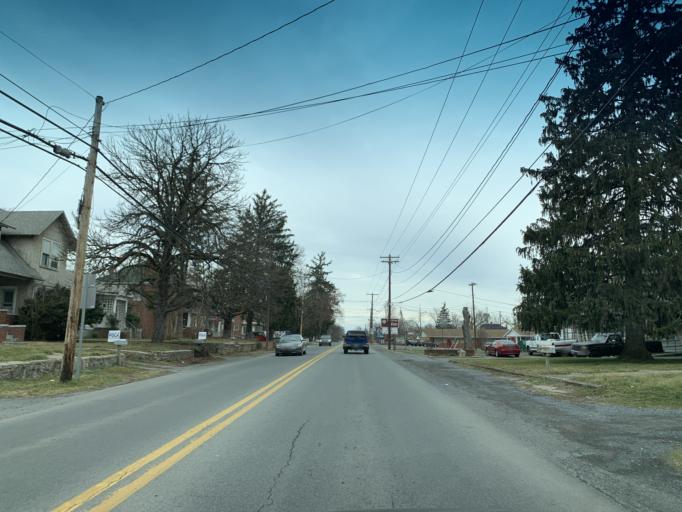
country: US
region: West Virginia
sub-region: Berkeley County
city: Martinsburg
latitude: 39.4435
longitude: -77.9815
